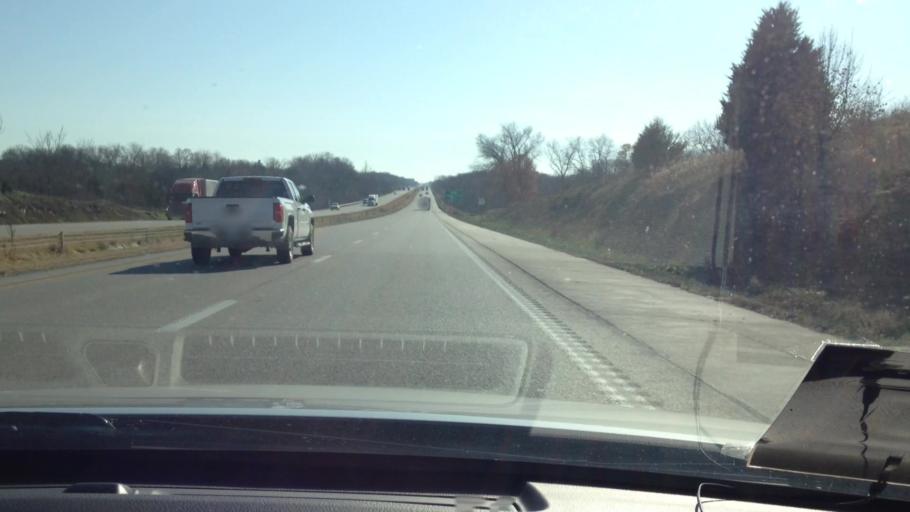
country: US
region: Missouri
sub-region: Platte County
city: Platte City
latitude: 39.4703
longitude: -94.7877
